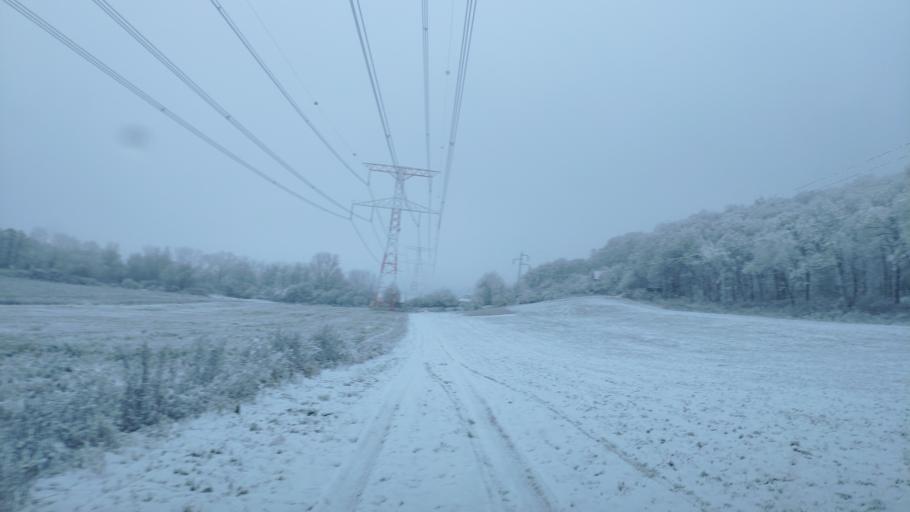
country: SK
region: Kosicky
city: Kosice
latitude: 48.6471
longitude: 21.1712
